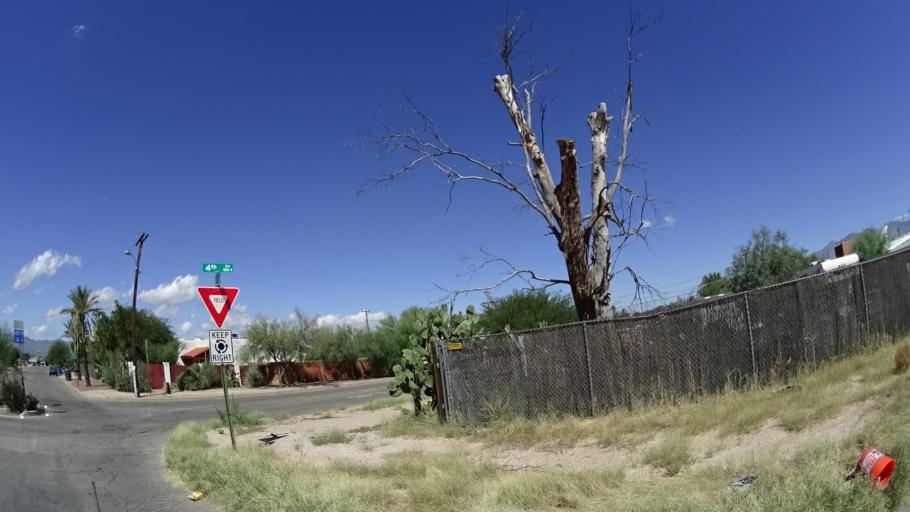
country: US
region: Arizona
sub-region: Pima County
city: South Tucson
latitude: 32.2436
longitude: -110.9655
